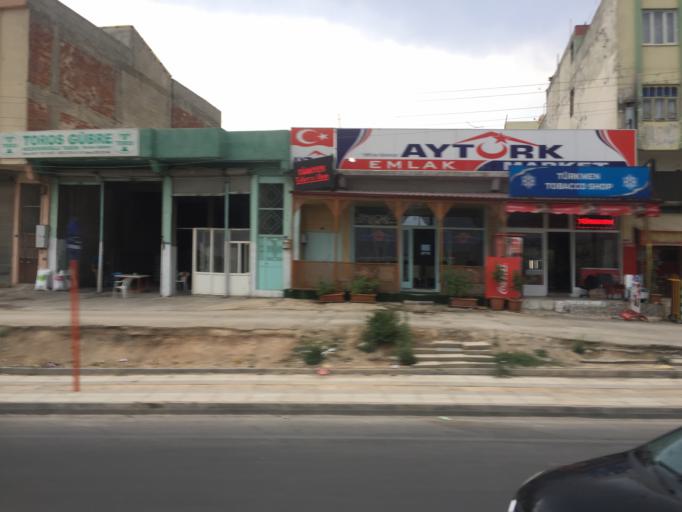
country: TR
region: Gaziantep
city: Gaziantep
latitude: 37.0403
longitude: 37.4239
